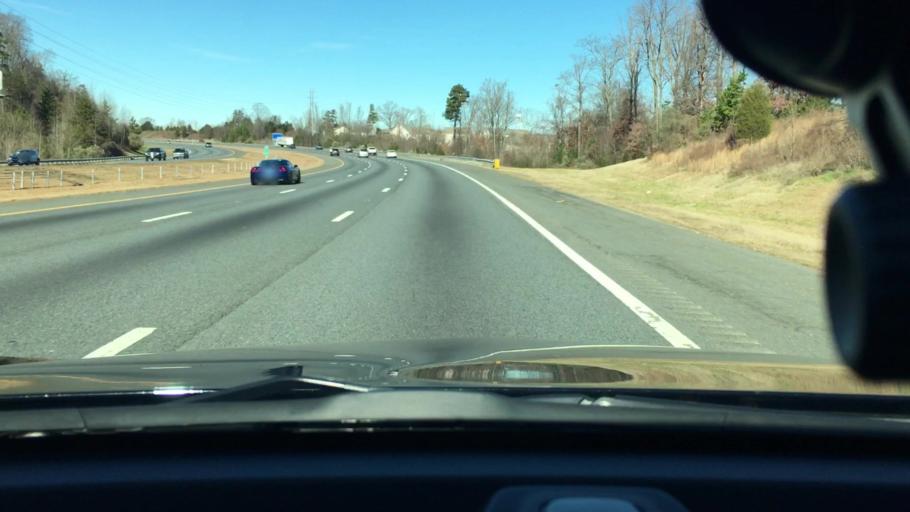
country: US
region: North Carolina
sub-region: Cabarrus County
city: Harrisburg
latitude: 35.3013
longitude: -80.6854
